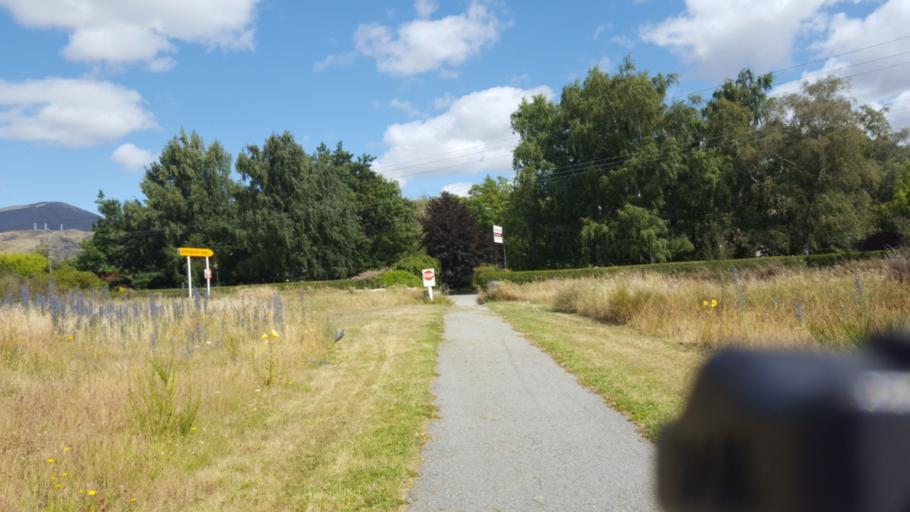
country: NZ
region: Otago
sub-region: Queenstown-Lakes District
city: Wanaka
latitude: -45.0388
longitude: 169.1824
